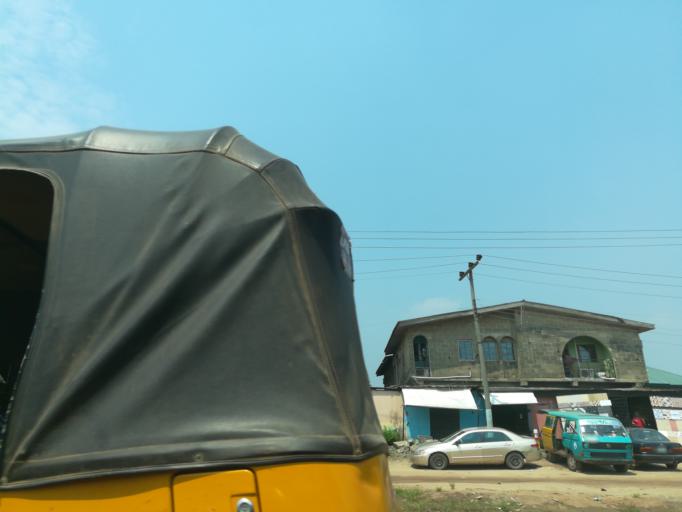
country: NG
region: Lagos
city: Ikorodu
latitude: 6.6371
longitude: 3.4818
